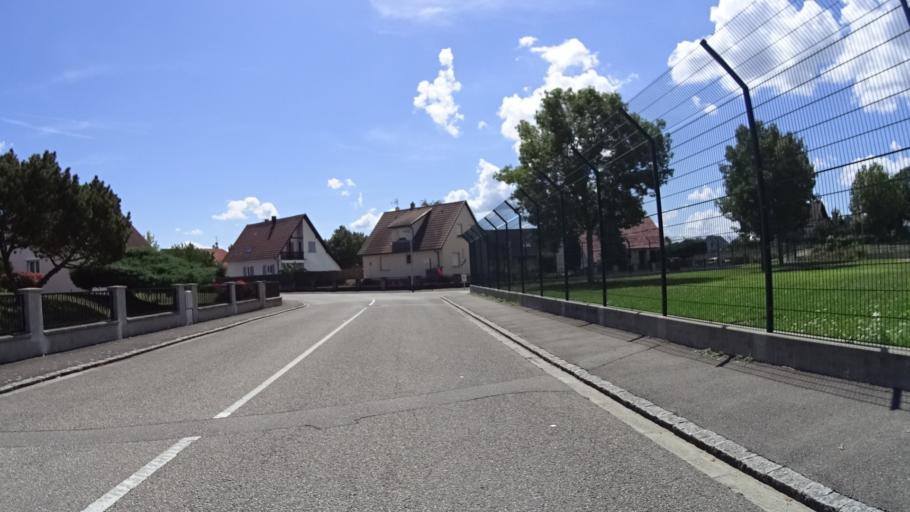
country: FR
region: Alsace
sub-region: Departement du Haut-Rhin
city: Ottmarsheim
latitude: 47.7856
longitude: 7.5030
